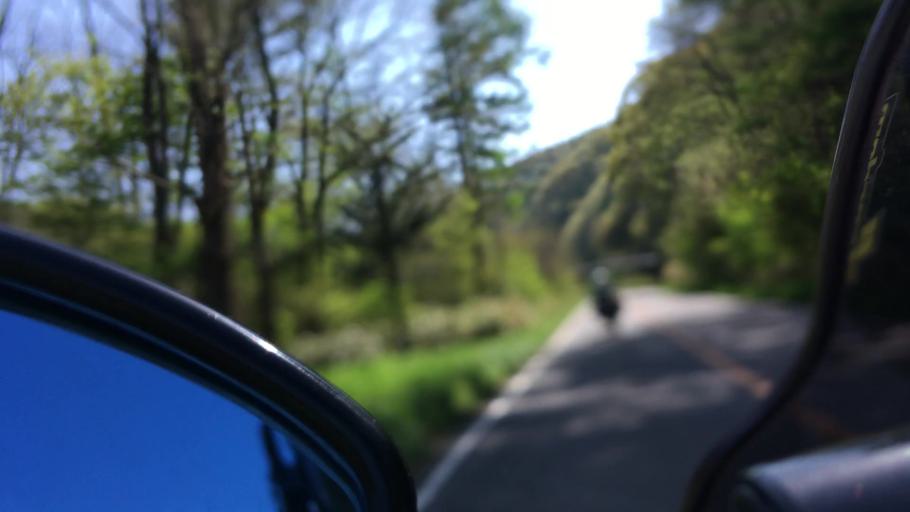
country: JP
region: Nagano
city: Komoro
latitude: 36.4917
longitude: 138.4898
